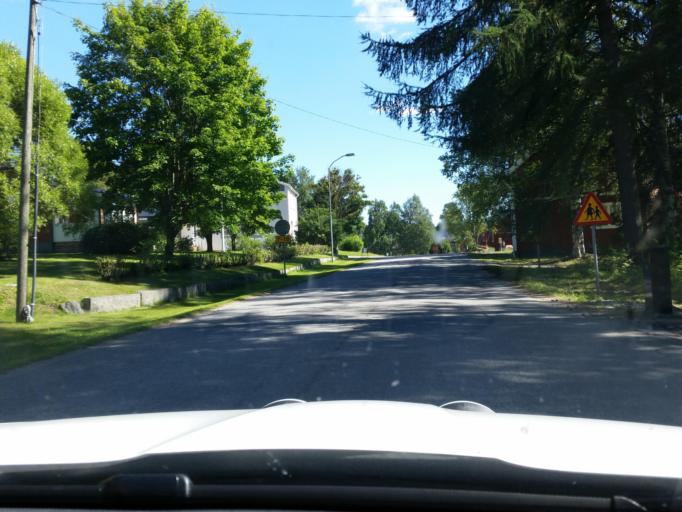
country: SE
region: Norrbotten
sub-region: Pitea Kommun
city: Bergsviken
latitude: 65.3075
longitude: 21.3785
